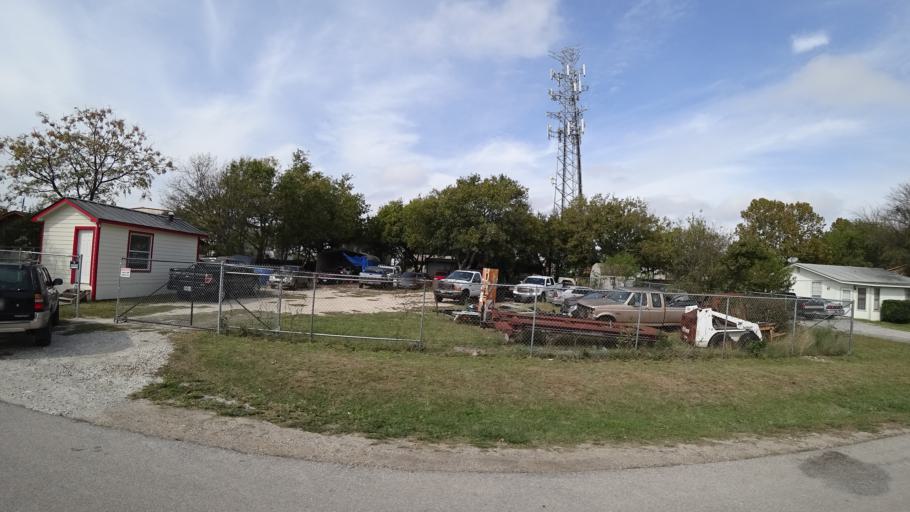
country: US
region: Texas
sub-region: Travis County
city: Wells Branch
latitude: 30.4533
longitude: -97.6685
